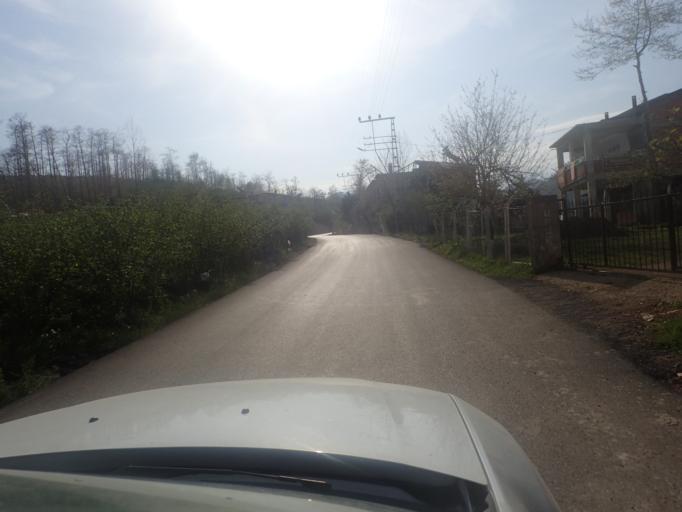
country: TR
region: Ordu
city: Catalpinar
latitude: 40.8858
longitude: 37.4918
